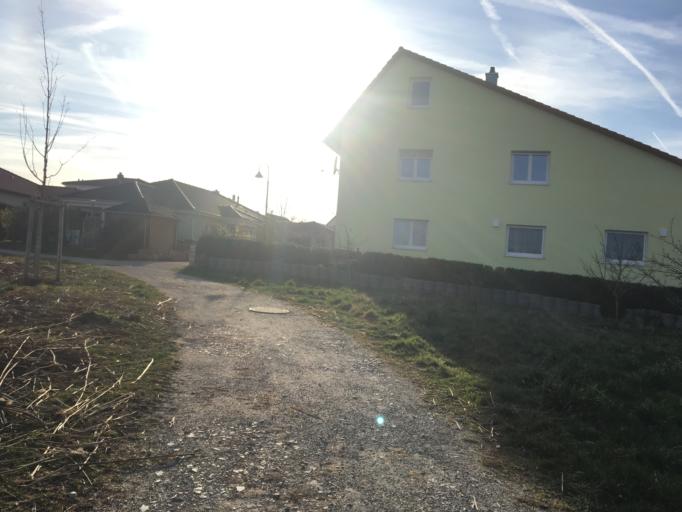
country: DE
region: Bavaria
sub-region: Regierungsbezirk Mittelfranken
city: Wilhermsdorf
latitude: 49.4761
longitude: 10.7245
